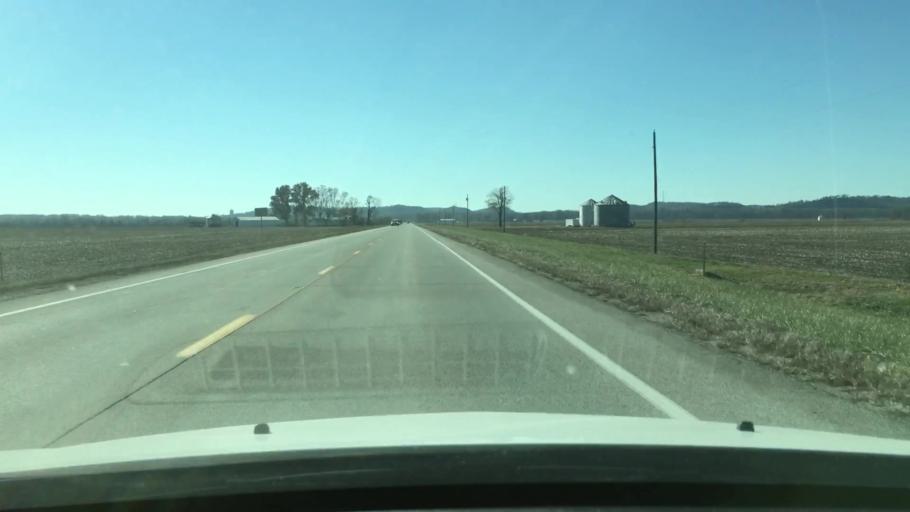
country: US
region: Missouri
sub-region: Pike County
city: Louisiana
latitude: 39.4807
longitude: -91.0173
